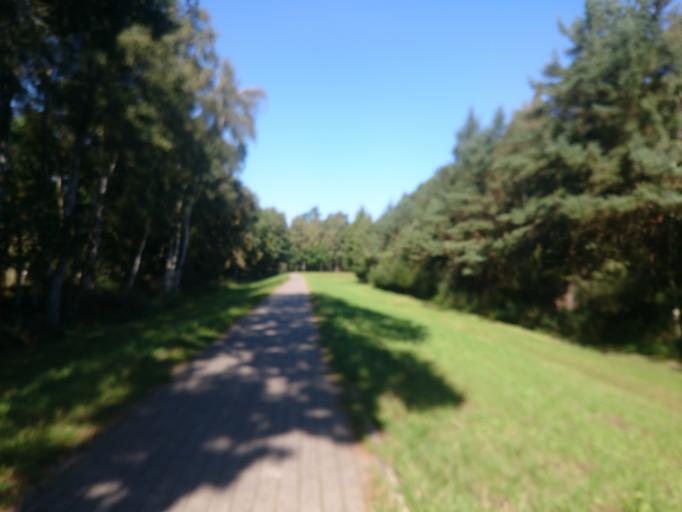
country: DE
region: Mecklenburg-Vorpommern
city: Zingst
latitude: 54.4312
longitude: 12.6640
